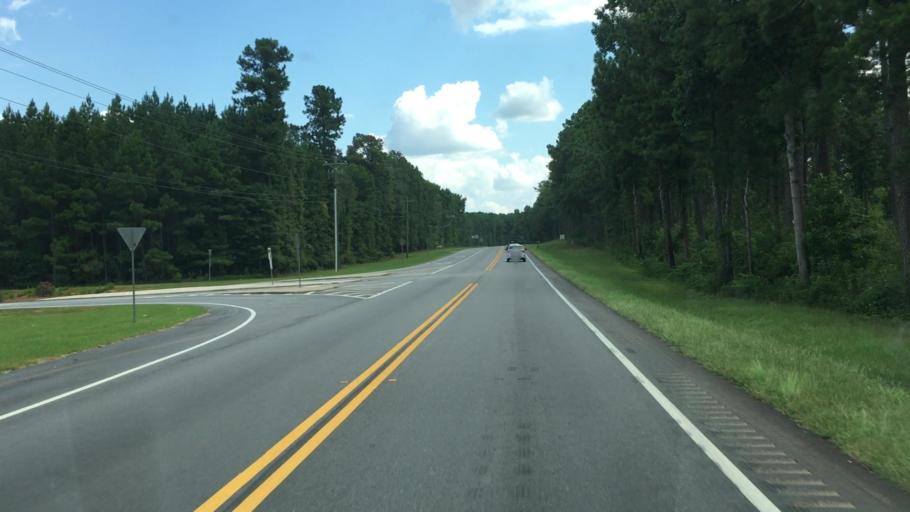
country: US
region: Georgia
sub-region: Putnam County
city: Jefferson
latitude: 33.4112
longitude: -83.3709
